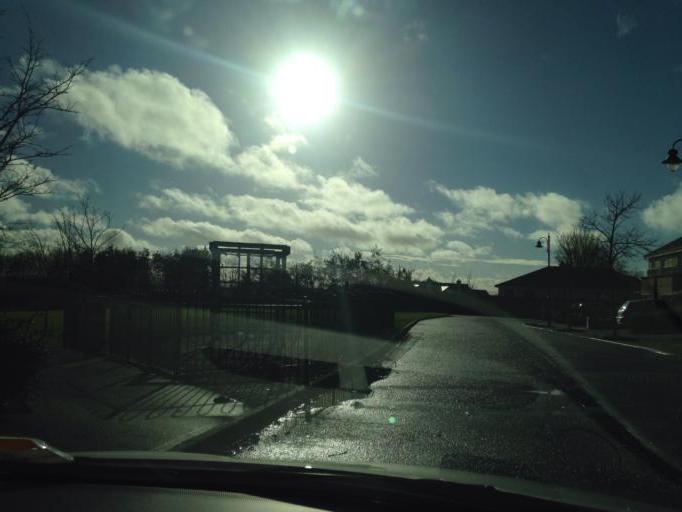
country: IE
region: Connaught
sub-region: County Galway
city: Oranmore
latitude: 53.2755
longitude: -8.9710
